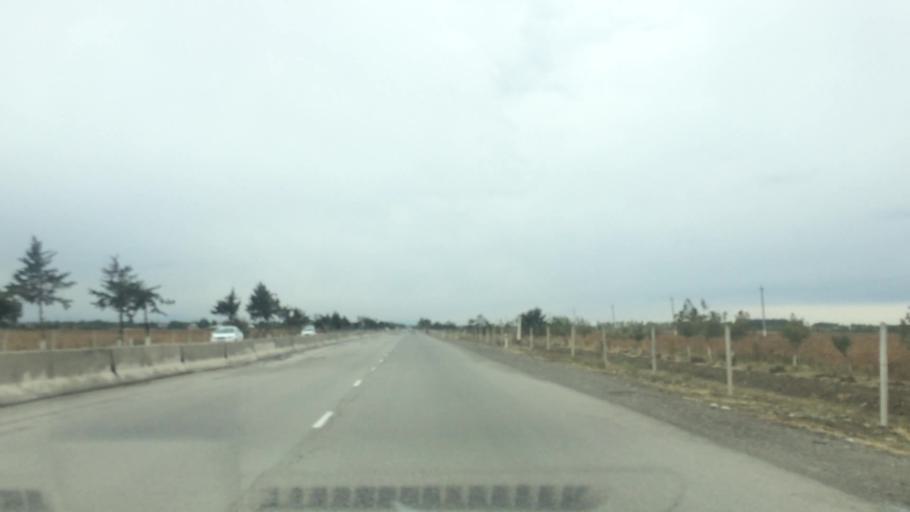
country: UZ
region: Samarqand
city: Bulung'ur
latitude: 39.7930
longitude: 67.3247
